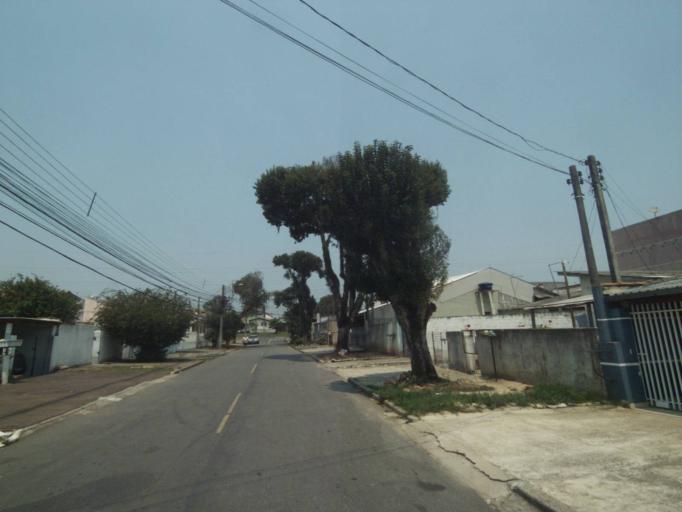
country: BR
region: Parana
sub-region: Sao Jose Dos Pinhais
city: Sao Jose dos Pinhais
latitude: -25.5278
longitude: -49.2449
